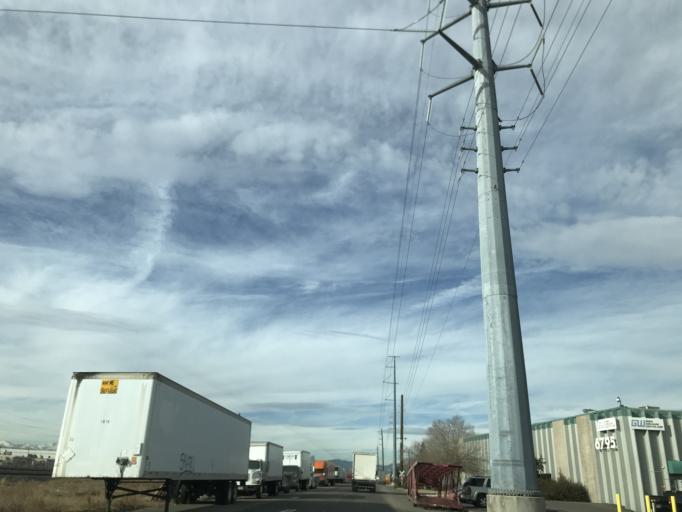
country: US
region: Colorado
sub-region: Adams County
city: Commerce City
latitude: 39.7735
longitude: -104.9092
